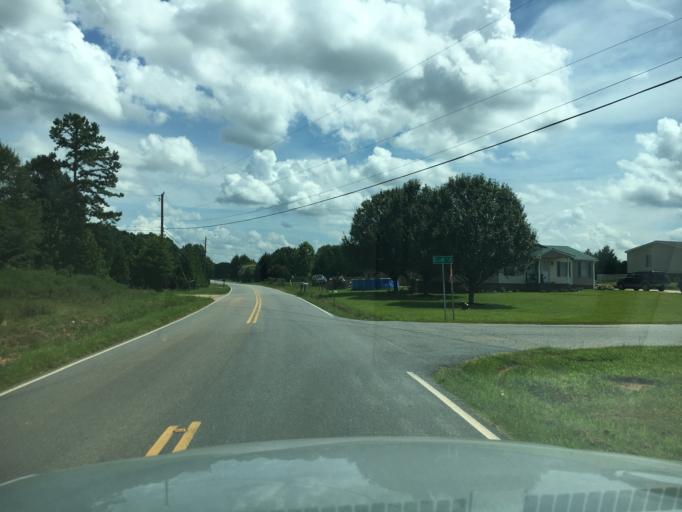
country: US
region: South Carolina
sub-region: Anderson County
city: Belton
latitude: 34.5578
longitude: -82.4690
